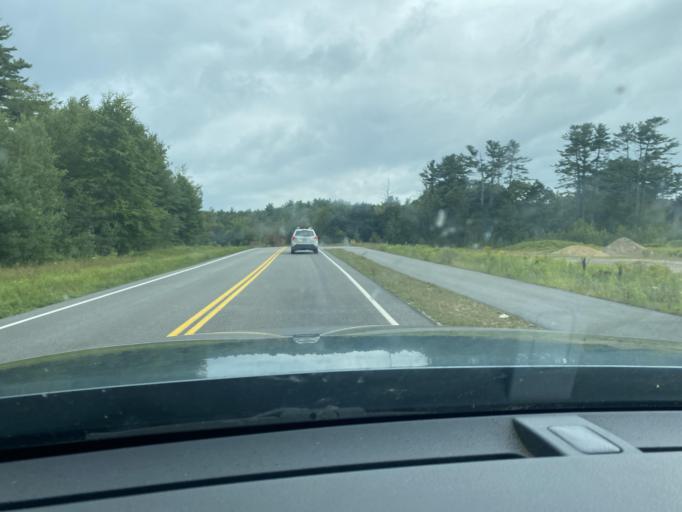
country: US
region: Maine
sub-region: York County
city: York Beach
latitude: 43.1748
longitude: -70.6183
